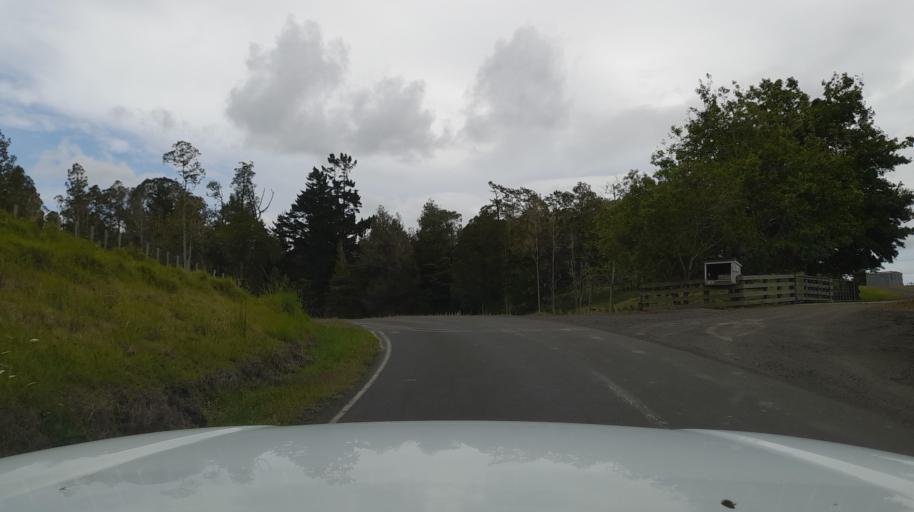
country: NZ
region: Northland
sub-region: Far North District
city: Kaitaia
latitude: -35.3073
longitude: 173.3432
